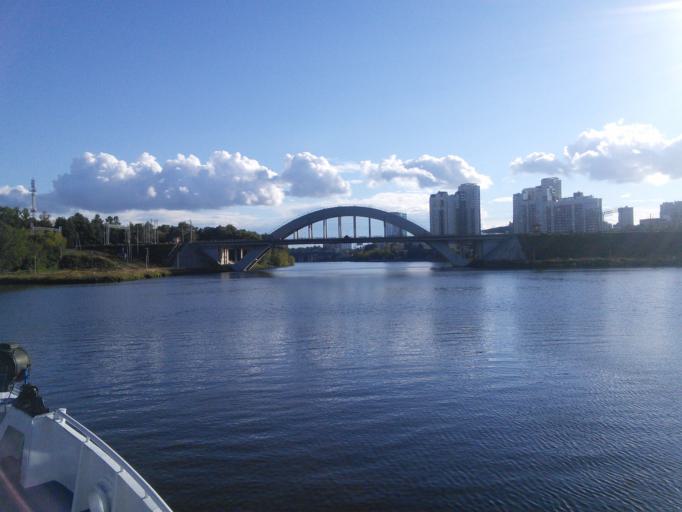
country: RU
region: Moskovskaya
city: Levoberezhnaya
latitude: 55.8918
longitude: 37.4656
